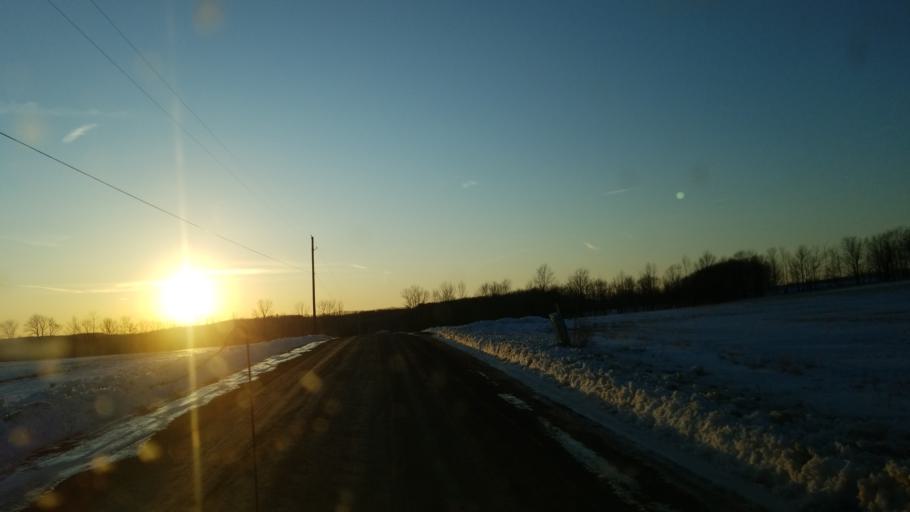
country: US
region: Pennsylvania
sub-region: Tioga County
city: Westfield
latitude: 42.0394
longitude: -77.6074
